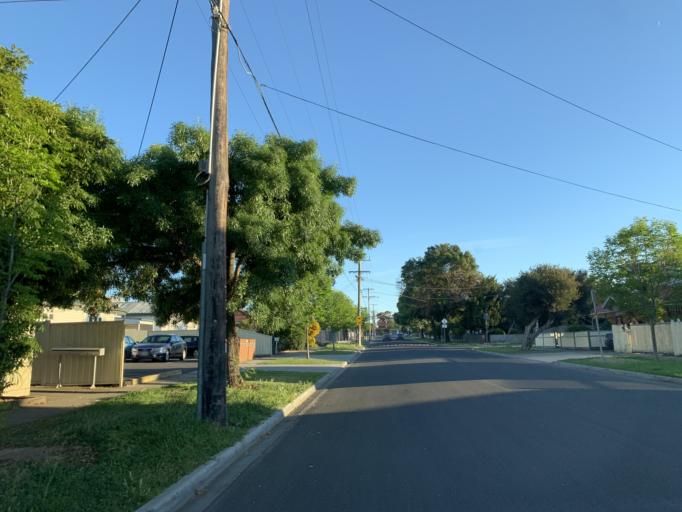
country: AU
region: Victoria
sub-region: Brimbank
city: St Albans
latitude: -37.7469
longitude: 144.8042
